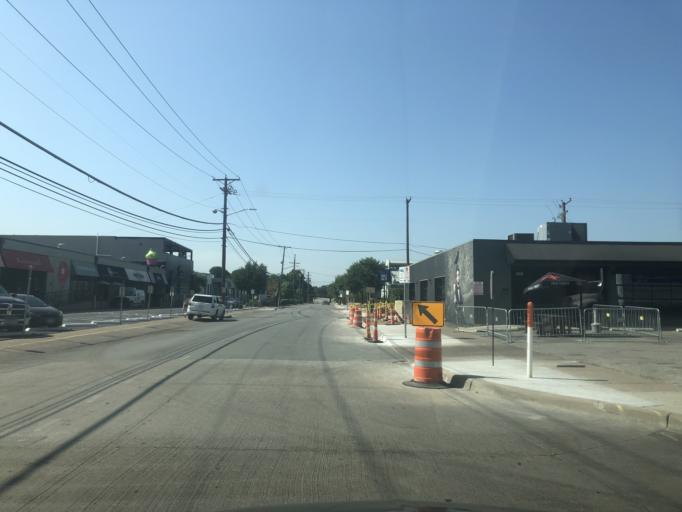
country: US
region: Texas
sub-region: Tarrant County
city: Fort Worth
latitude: 32.7501
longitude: -97.3566
